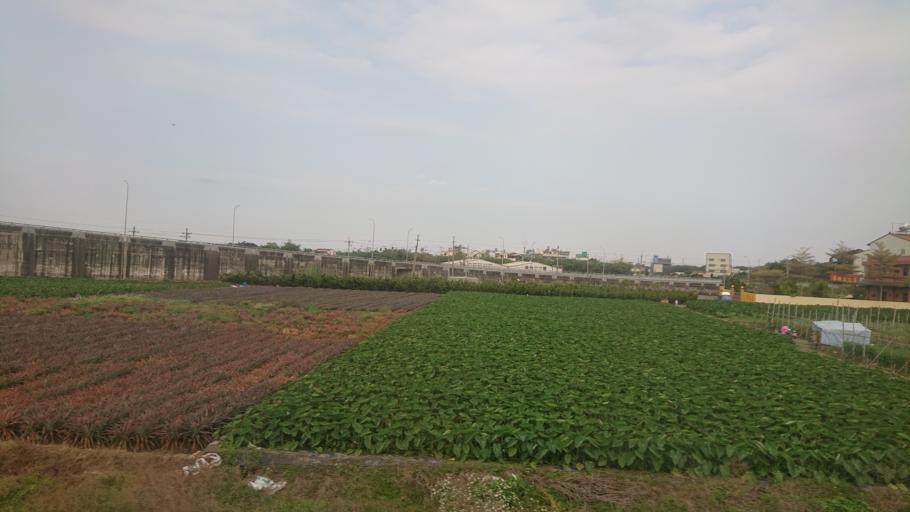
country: TW
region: Taiwan
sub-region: Yunlin
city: Douliu
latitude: 23.7574
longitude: 120.6115
